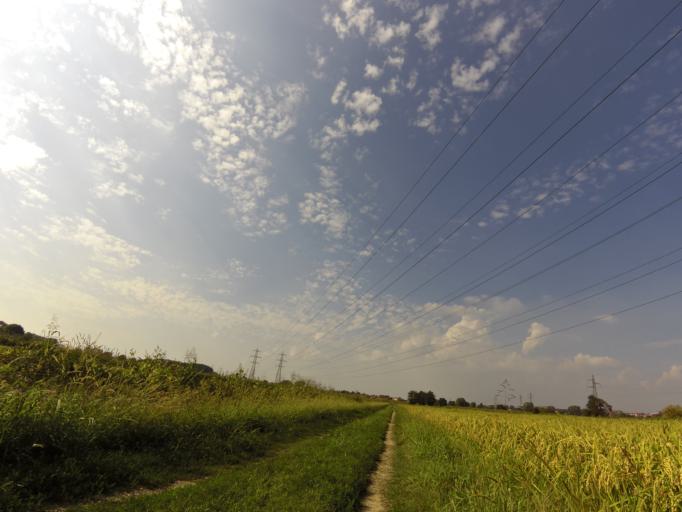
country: IT
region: Lombardy
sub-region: Citta metropolitana di Milano
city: Civesio
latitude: 45.3879
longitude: 9.2760
